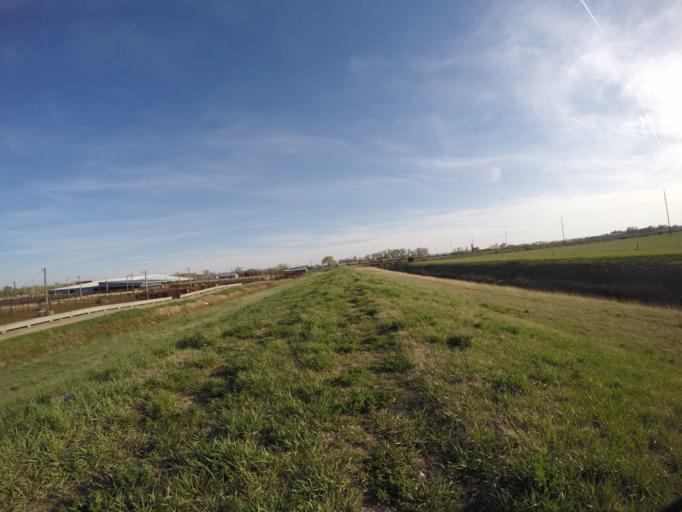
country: US
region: Kansas
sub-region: Saline County
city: Salina
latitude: 38.8473
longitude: -97.6304
